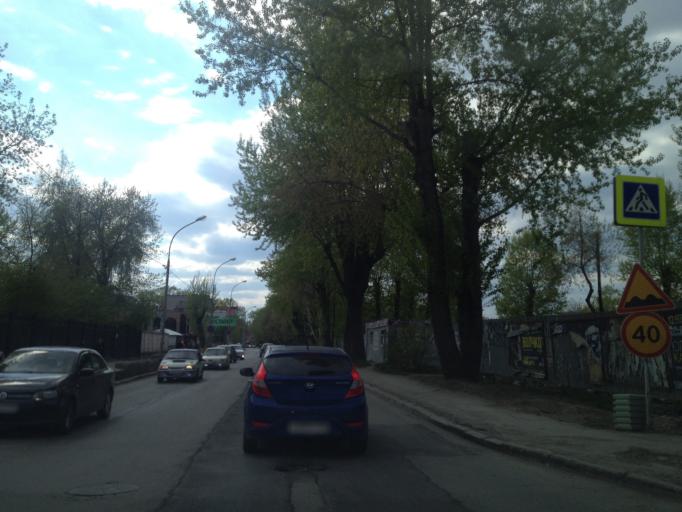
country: RU
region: Sverdlovsk
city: Yekaterinburg
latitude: 56.8573
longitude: 60.5972
